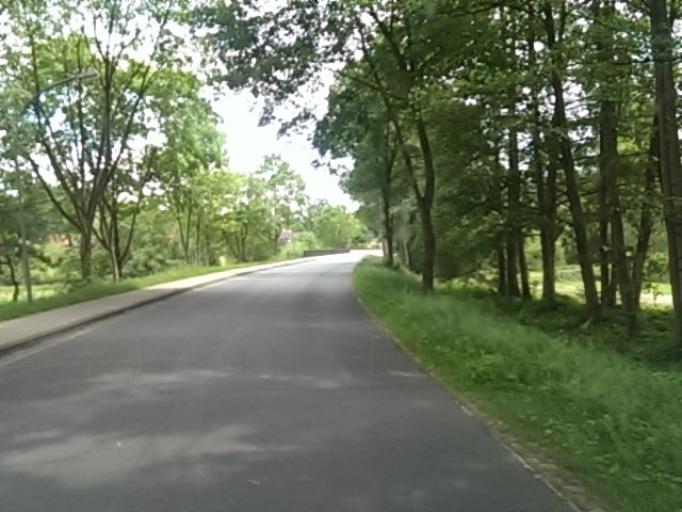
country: DE
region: Lower Saxony
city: Hermannsburg
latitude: 52.7991
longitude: 10.0857
